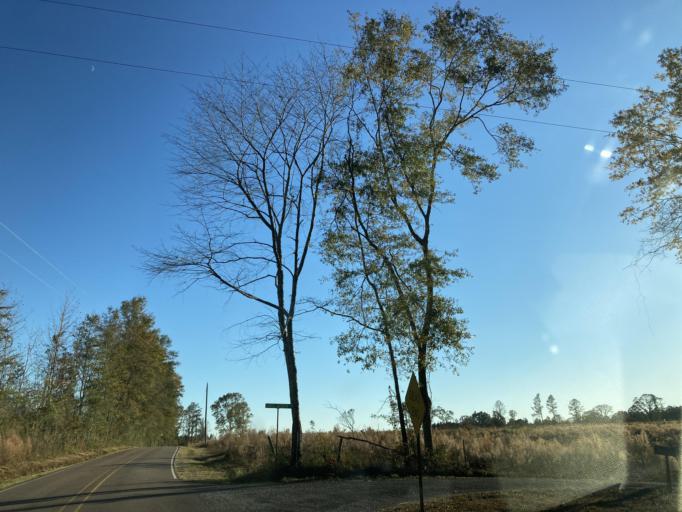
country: US
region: Mississippi
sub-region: Lamar County
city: Sumrall
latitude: 31.2628
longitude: -89.6031
